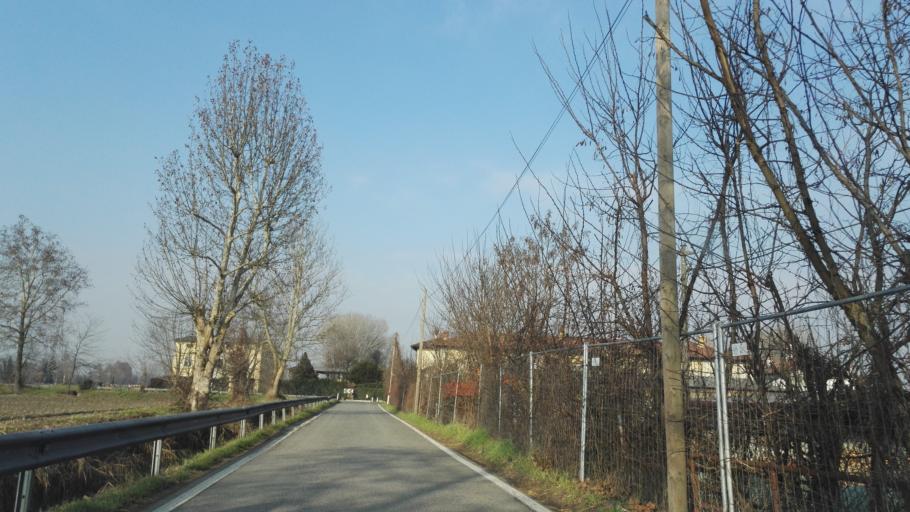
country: IT
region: Lombardy
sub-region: Citta metropolitana di Milano
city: Triginto
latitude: 45.4012
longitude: 9.3149
